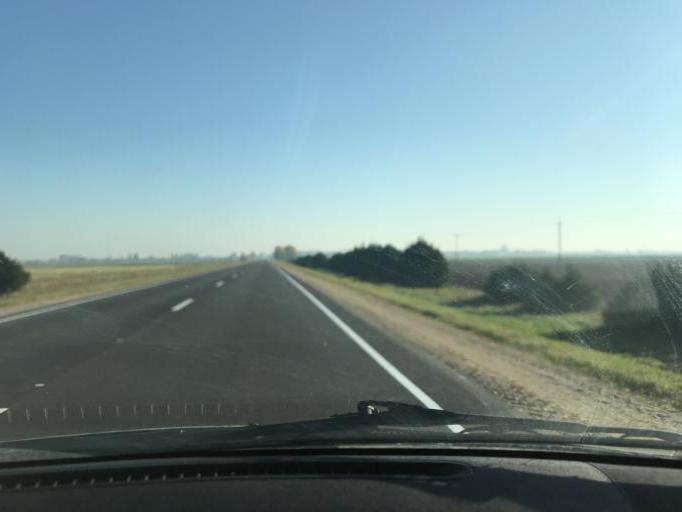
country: BY
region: Brest
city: Baranovichi
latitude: 52.8916
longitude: 25.8271
